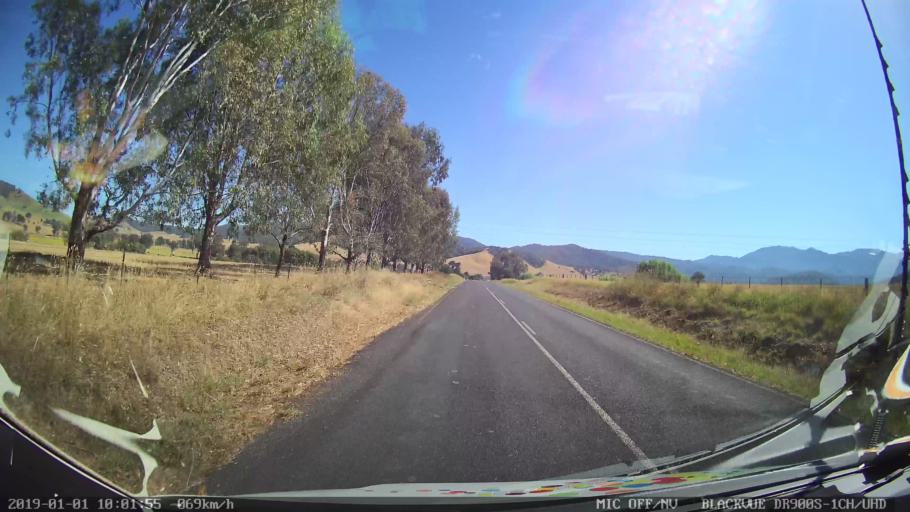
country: AU
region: New South Wales
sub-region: Snowy River
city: Jindabyne
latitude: -36.1864
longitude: 148.1011
